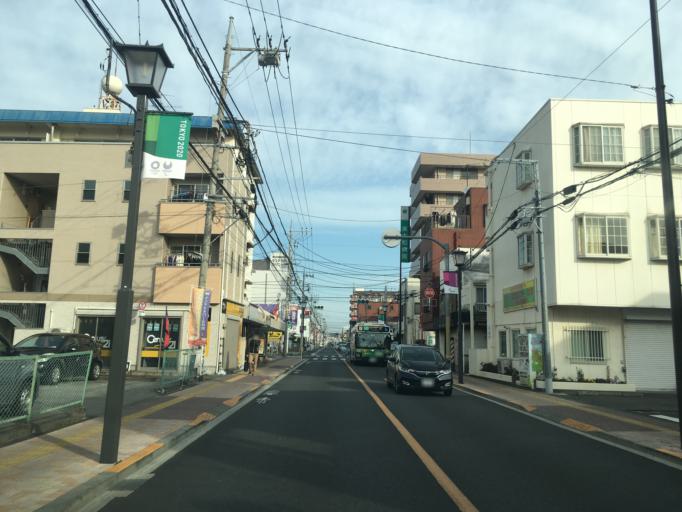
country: JP
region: Tokyo
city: Higashimurayama-shi
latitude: 35.7403
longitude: 139.4317
